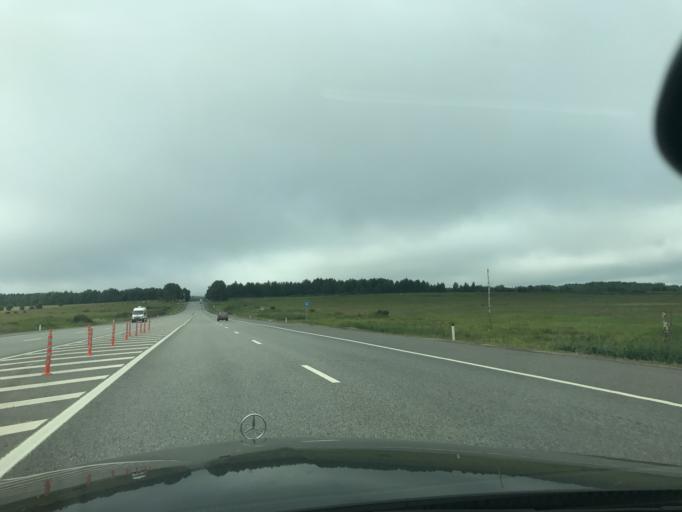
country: RU
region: Smolensk
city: Vyaz'ma
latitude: 55.3366
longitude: 34.5918
